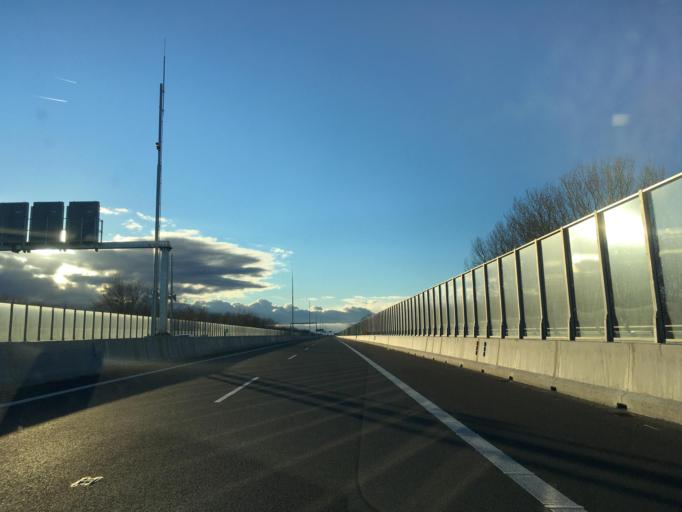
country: SK
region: Bratislavsky
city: Bratislava
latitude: 48.0878
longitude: 17.1684
